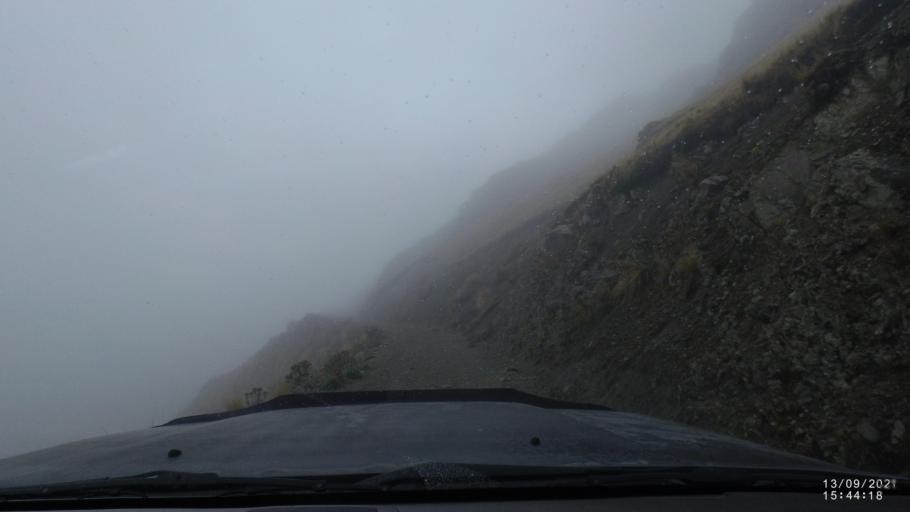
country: BO
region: Cochabamba
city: Colomi
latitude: -17.3209
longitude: -65.7212
